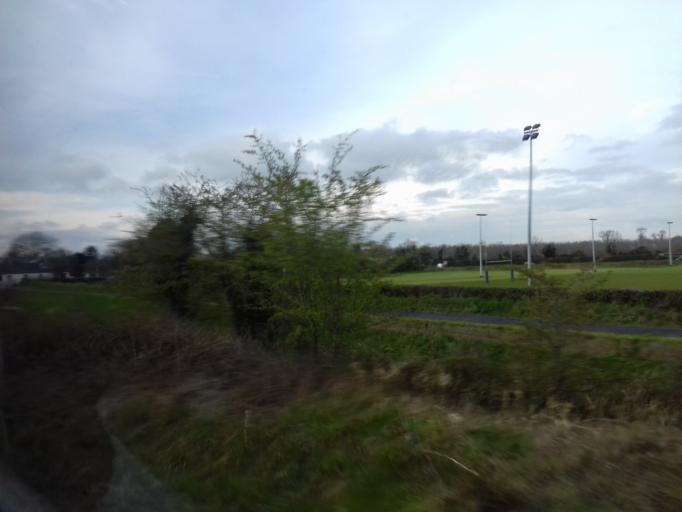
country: IE
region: Leinster
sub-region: Kildare
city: Kilcock
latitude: 53.3908
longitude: -6.6463
